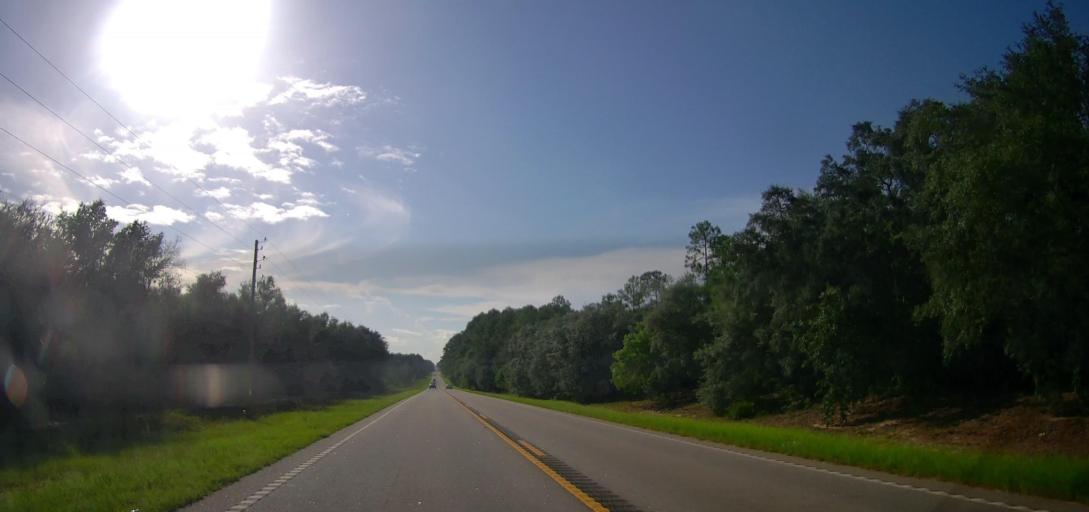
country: US
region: Georgia
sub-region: Coffee County
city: Douglas
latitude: 31.4639
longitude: -82.7555
